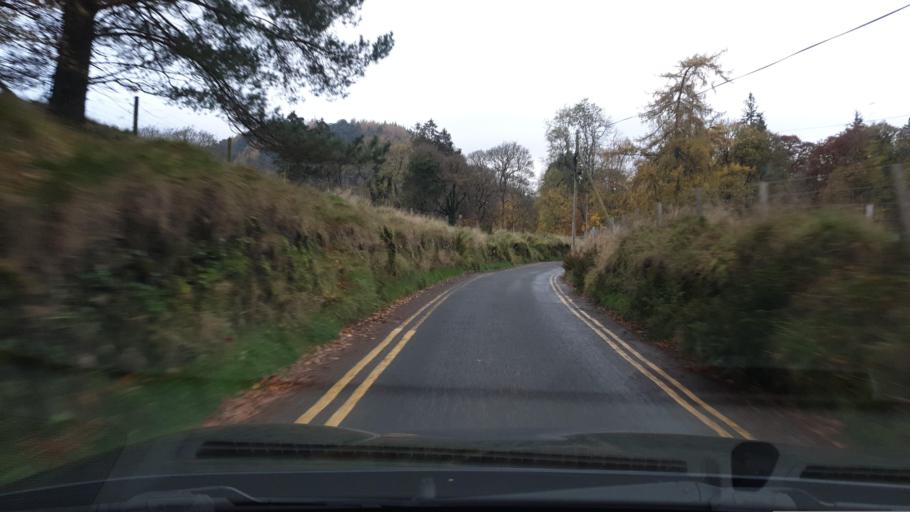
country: IE
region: Leinster
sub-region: Wicklow
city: Rathdrum
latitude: 53.0115
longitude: -6.3276
